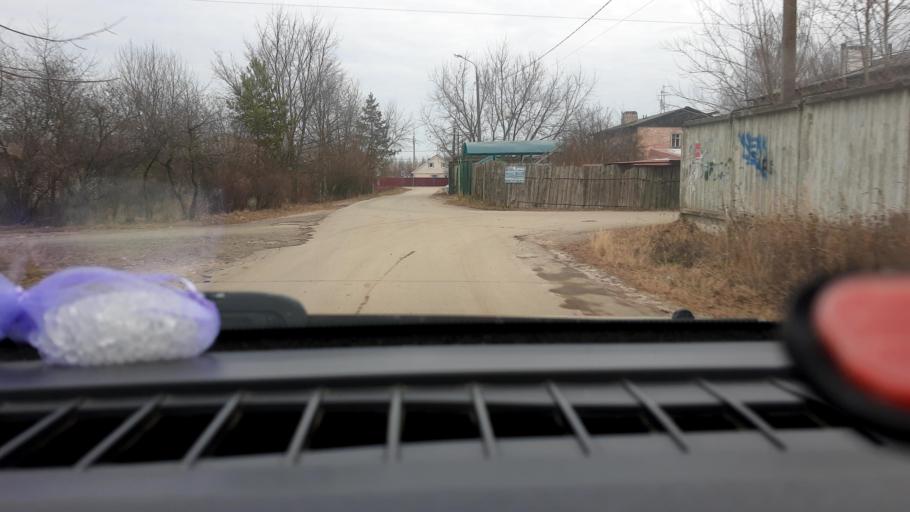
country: RU
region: Nizjnij Novgorod
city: Gorbatovka
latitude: 56.3839
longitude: 43.7798
